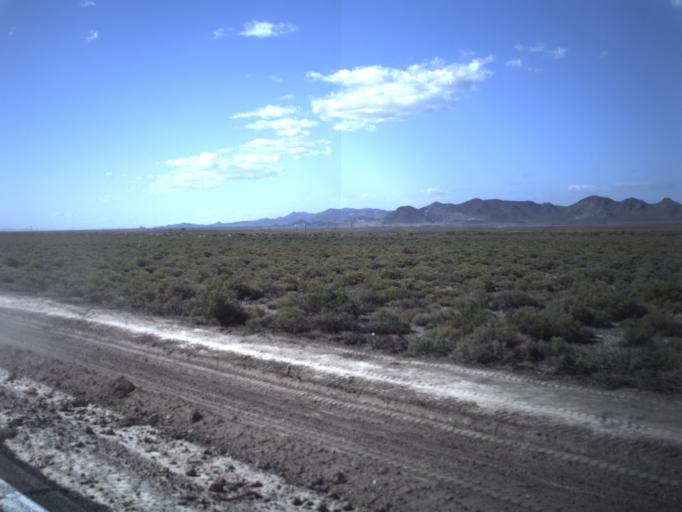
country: US
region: Utah
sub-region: Beaver County
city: Milford
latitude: 38.5195
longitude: -112.9912
